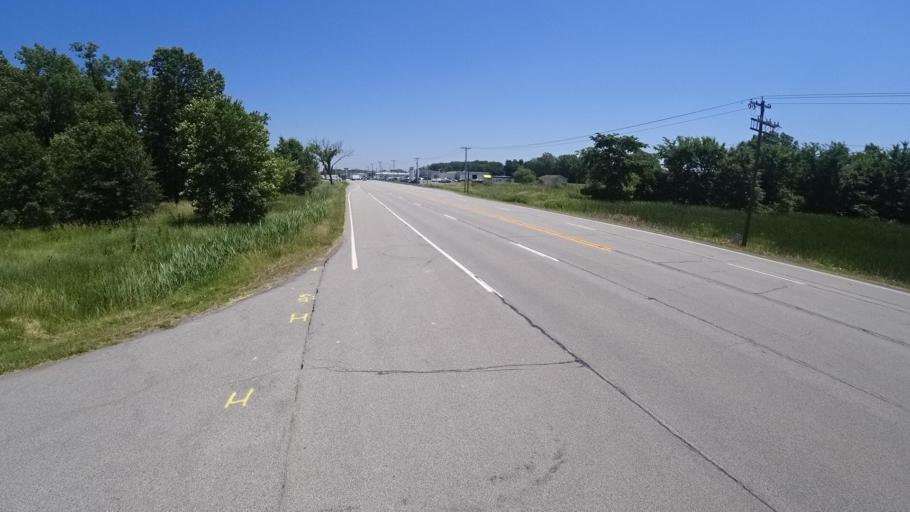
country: US
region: Indiana
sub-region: Porter County
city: Burns Harbor
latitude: 41.6029
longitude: -87.1189
